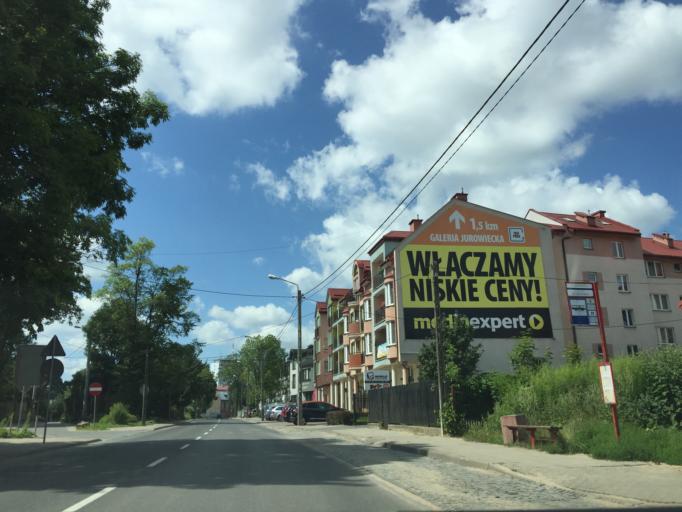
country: PL
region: Podlasie
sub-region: Bialystok
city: Bialystok
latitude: 53.1348
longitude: 23.1815
